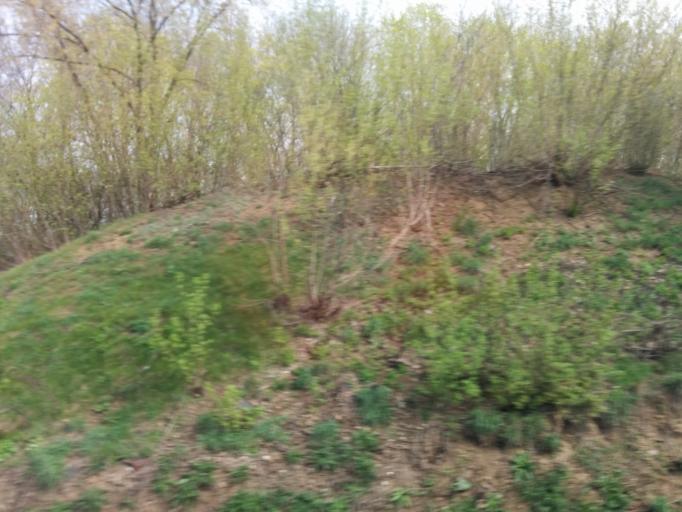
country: RU
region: Tambov
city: Tambov
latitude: 52.7545
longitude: 41.3872
